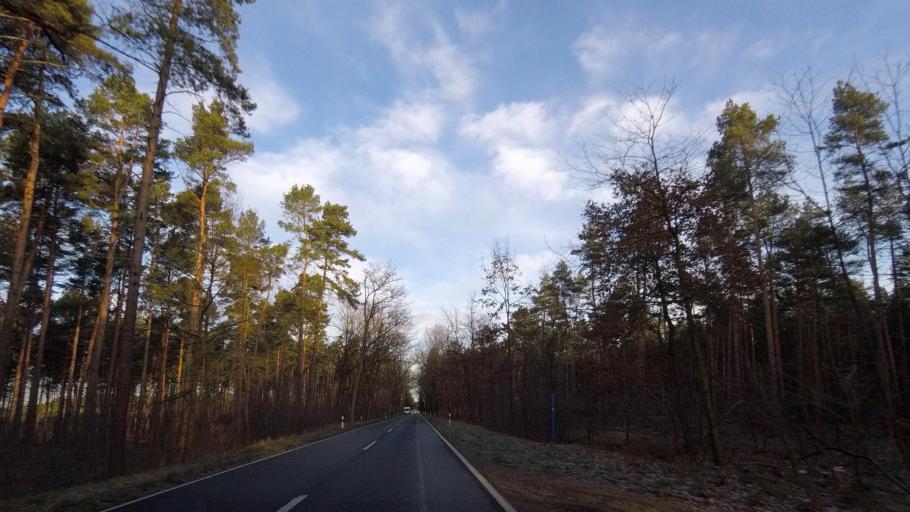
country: DE
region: Brandenburg
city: Niedergorsdorf
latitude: 52.0419
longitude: 12.9432
